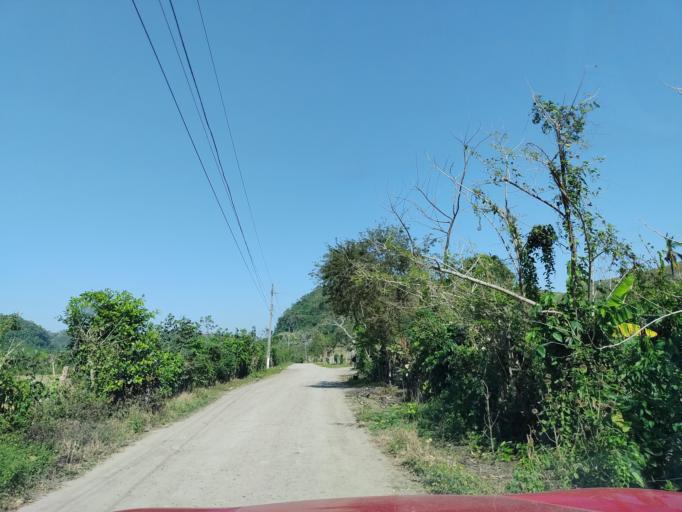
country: MX
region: Veracruz
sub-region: Papantla
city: Polutla
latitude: 20.4854
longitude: -97.1902
